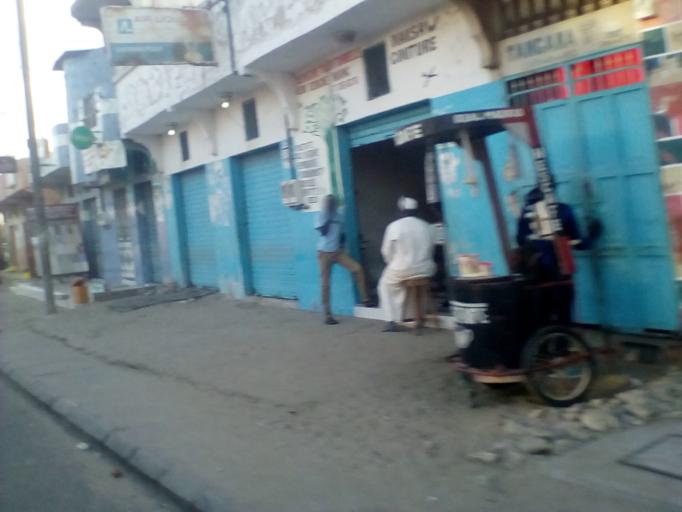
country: SN
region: Saint-Louis
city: Saint-Louis
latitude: 16.0222
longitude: -16.4915
